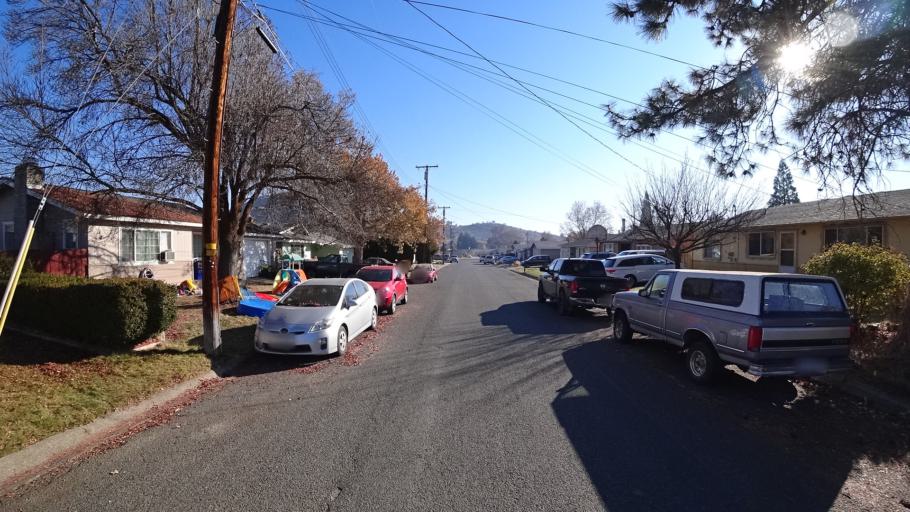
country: US
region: California
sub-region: Siskiyou County
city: Yreka
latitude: 41.7201
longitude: -122.6435
